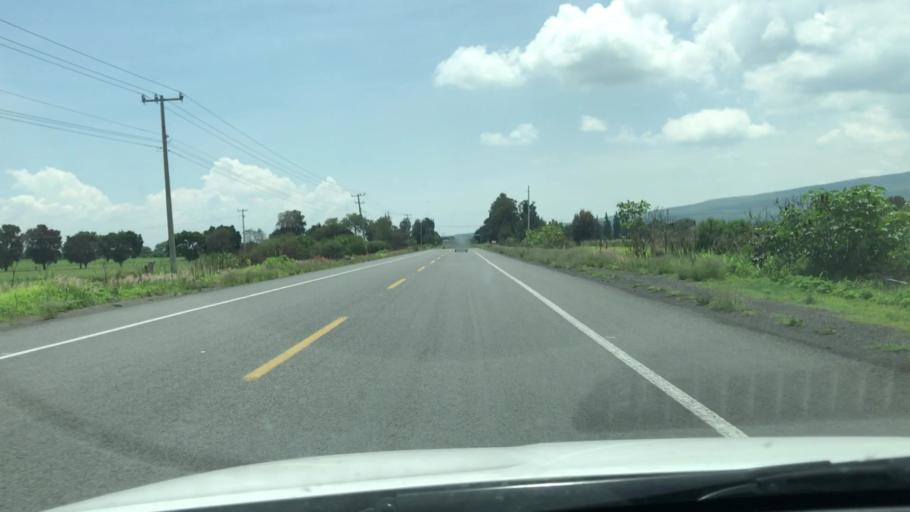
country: MX
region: Michoacan
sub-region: Yurecuaro
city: Yurecuaro
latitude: 20.3394
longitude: -102.1800
